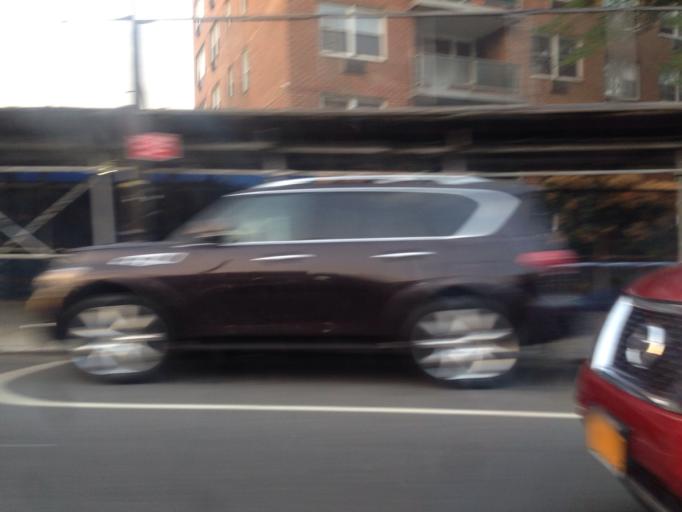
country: US
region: New York
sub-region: Kings County
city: Brooklyn
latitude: 40.6304
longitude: -73.9450
